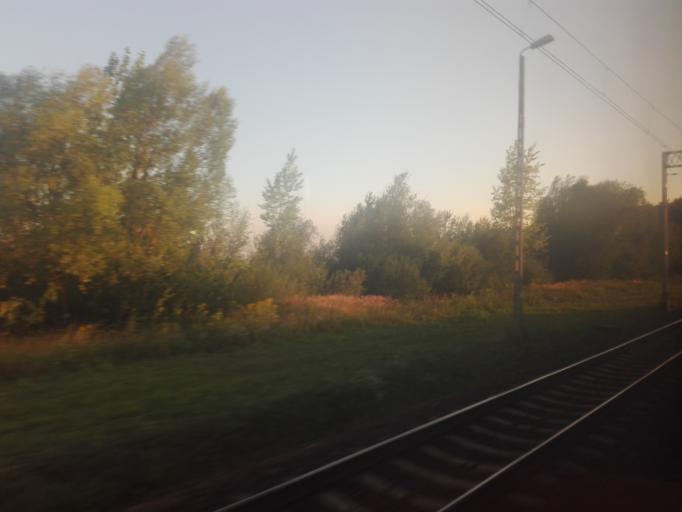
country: PL
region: Masovian Voivodeship
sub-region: Powiat warszawski zachodni
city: Blonie
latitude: 52.1865
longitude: 20.5961
